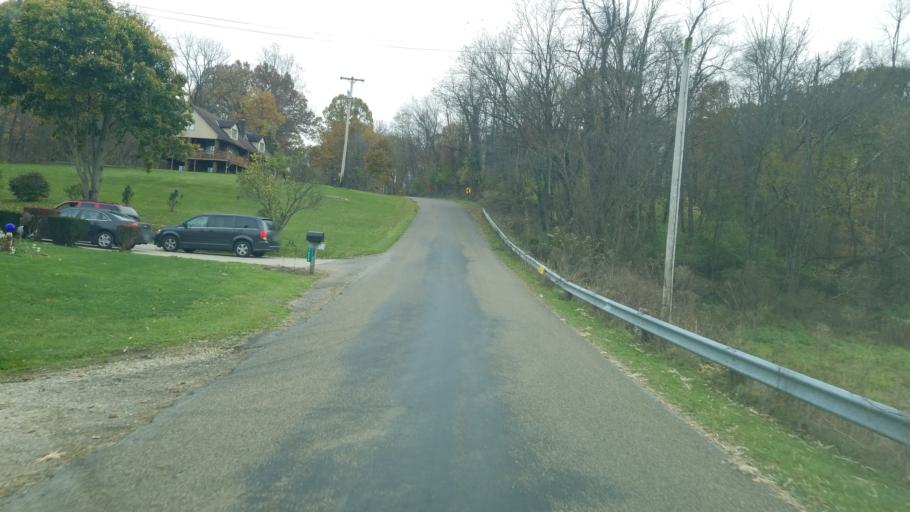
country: US
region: Ohio
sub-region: Richland County
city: Mansfield
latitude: 40.7179
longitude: -82.4959
